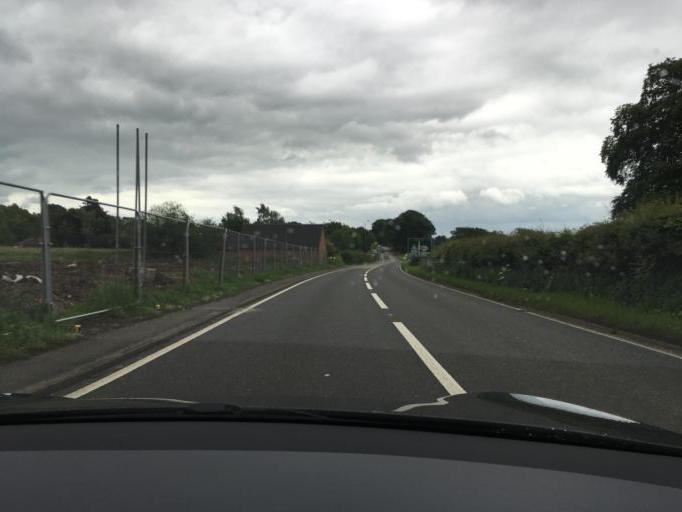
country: GB
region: England
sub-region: Derbyshire
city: Ashbourne
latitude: 52.9989
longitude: -1.7026
